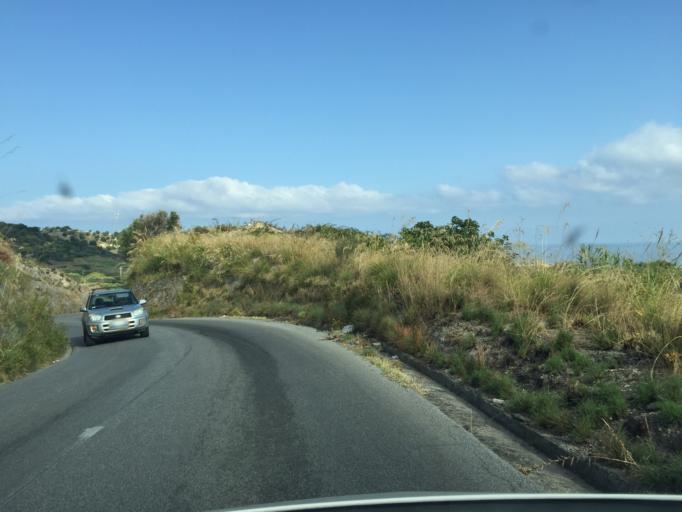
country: IT
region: Calabria
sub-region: Provincia di Vibo-Valentia
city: Briatico
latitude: 38.7168
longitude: 16.0481
